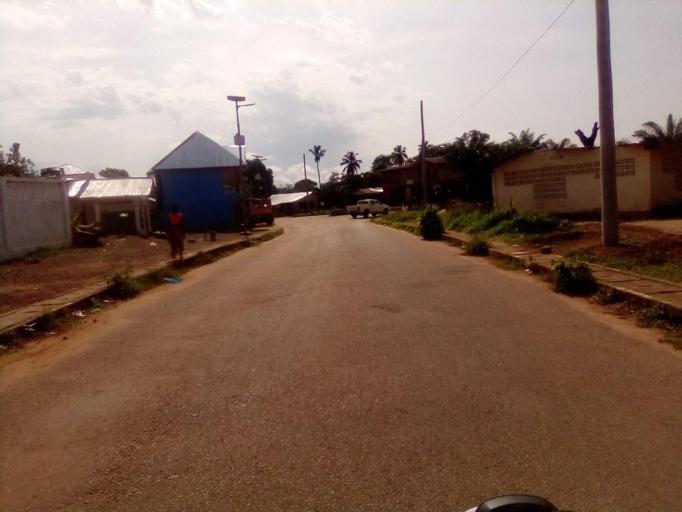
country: SL
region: Southern Province
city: Pujehun
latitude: 7.3574
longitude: -11.7165
